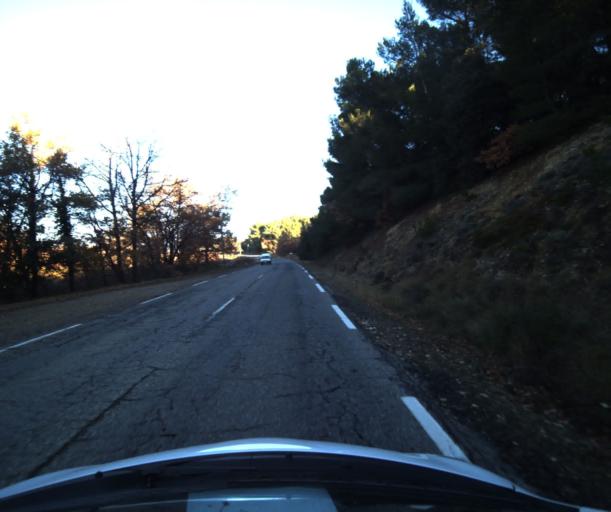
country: FR
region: Provence-Alpes-Cote d'Azur
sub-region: Departement du Vaucluse
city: Pertuis
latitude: 43.7214
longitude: 5.4993
